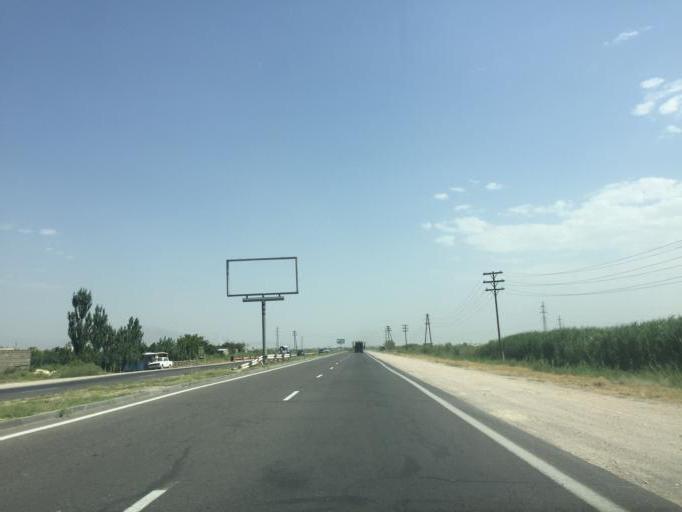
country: AM
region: Ararat
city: Shahumyan
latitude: 39.9317
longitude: 44.5684
